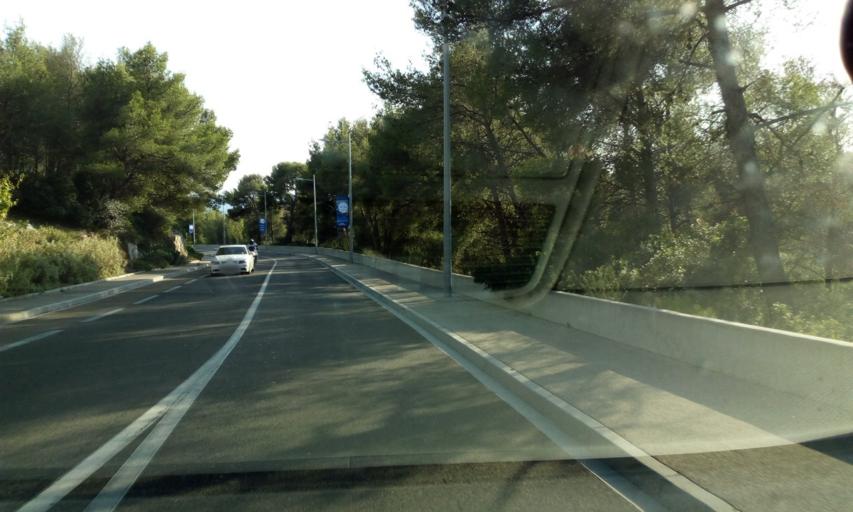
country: FR
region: Provence-Alpes-Cote d'Azur
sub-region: Departement du Var
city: Bandol
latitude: 43.1460
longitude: 5.7483
